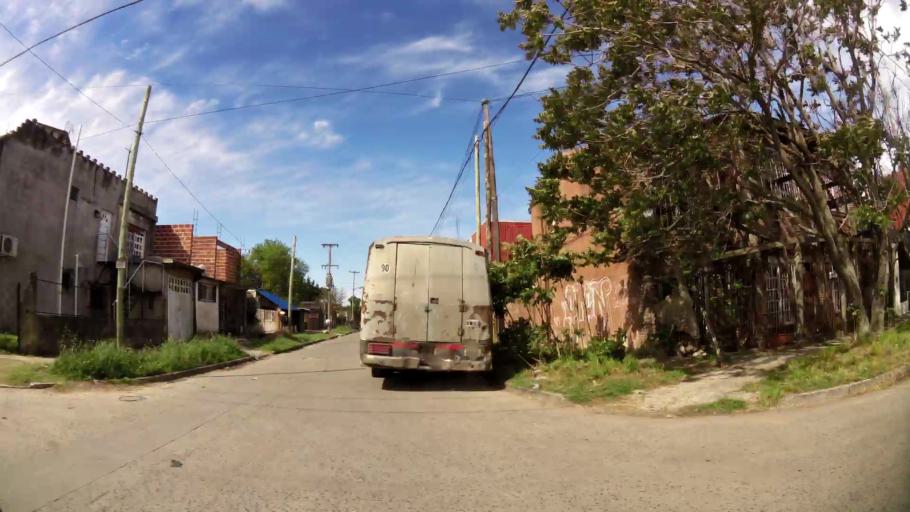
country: AR
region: Buenos Aires
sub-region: Partido de Quilmes
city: Quilmes
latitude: -34.7757
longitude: -58.3033
